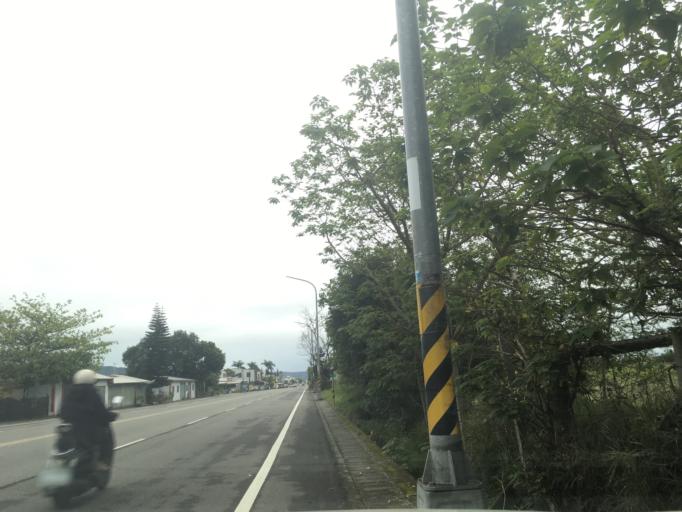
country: TW
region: Taiwan
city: Taitung City
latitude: 22.7646
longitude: 121.0553
